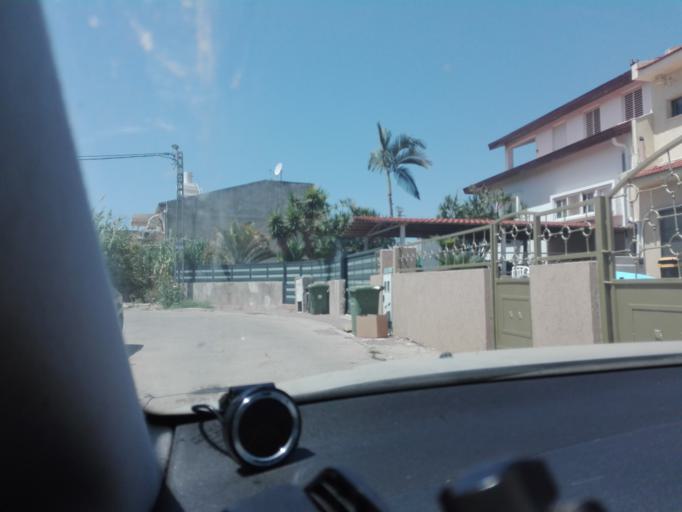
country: IL
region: Central District
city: Bene 'Ayish
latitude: 31.7343
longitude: 34.7469
